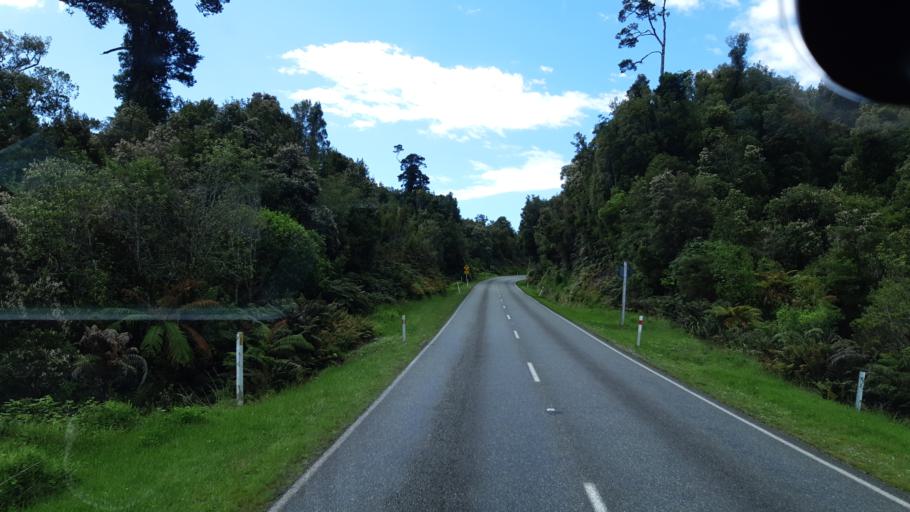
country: NZ
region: West Coast
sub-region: Westland District
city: Hokitika
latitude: -43.0491
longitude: 170.6379
